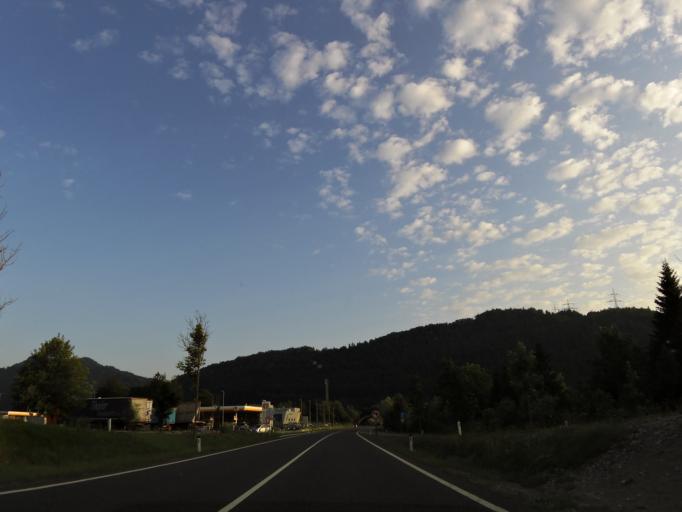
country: AT
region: Tyrol
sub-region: Politischer Bezirk Reutte
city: Musau
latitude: 47.5491
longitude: 10.6590
